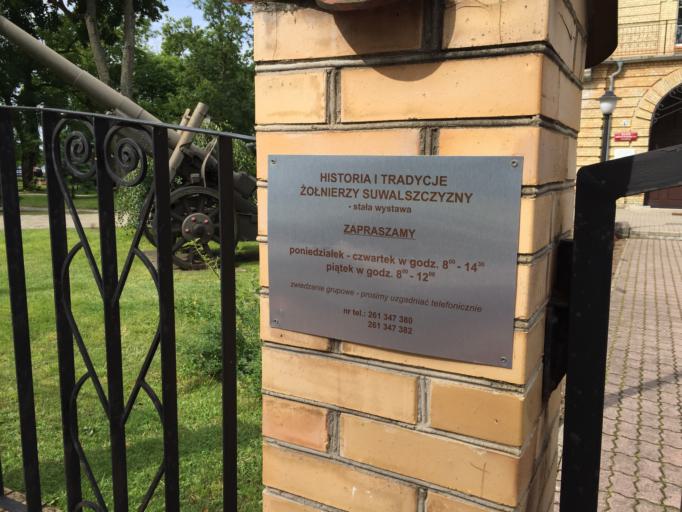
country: PL
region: Podlasie
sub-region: Suwalki
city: Suwalki
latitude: 54.0852
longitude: 22.9299
